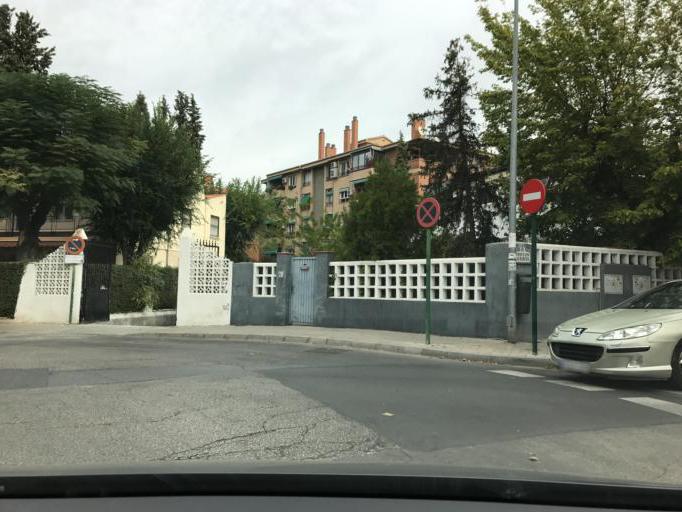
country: ES
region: Andalusia
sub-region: Provincia de Granada
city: Granada
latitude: 37.1660
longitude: -3.5921
